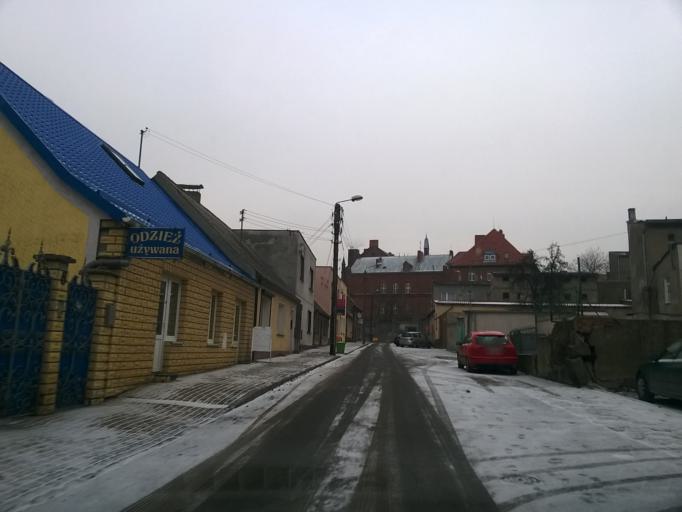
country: PL
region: Kujawsko-Pomorskie
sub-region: Powiat nakielski
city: Kcynia
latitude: 52.9922
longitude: 17.4868
